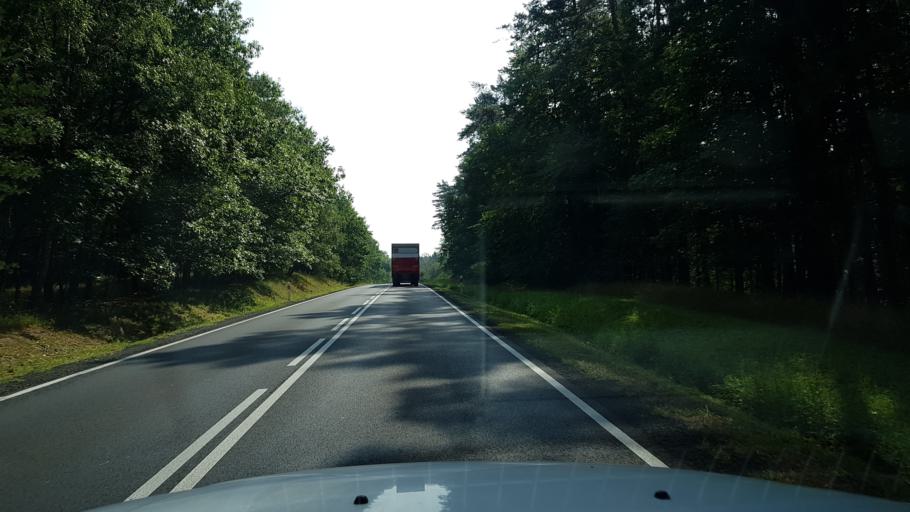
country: PL
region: West Pomeranian Voivodeship
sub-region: Powiat walecki
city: Miroslawiec
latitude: 53.3499
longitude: 16.1523
